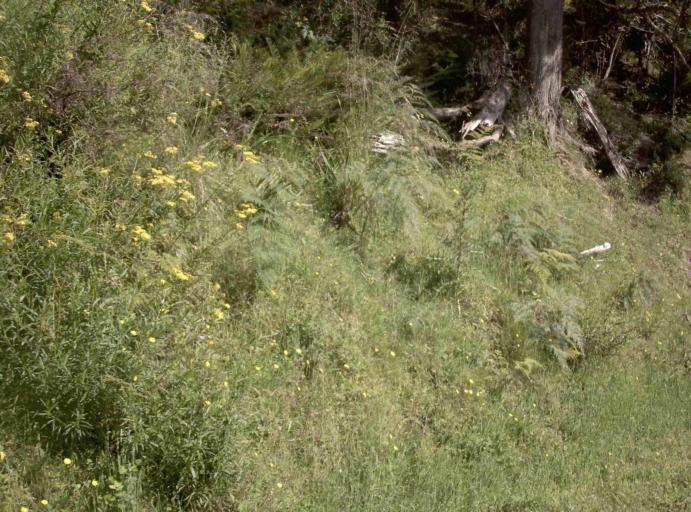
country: AU
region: New South Wales
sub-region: Bombala
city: Bombala
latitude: -37.3463
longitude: 148.6932
